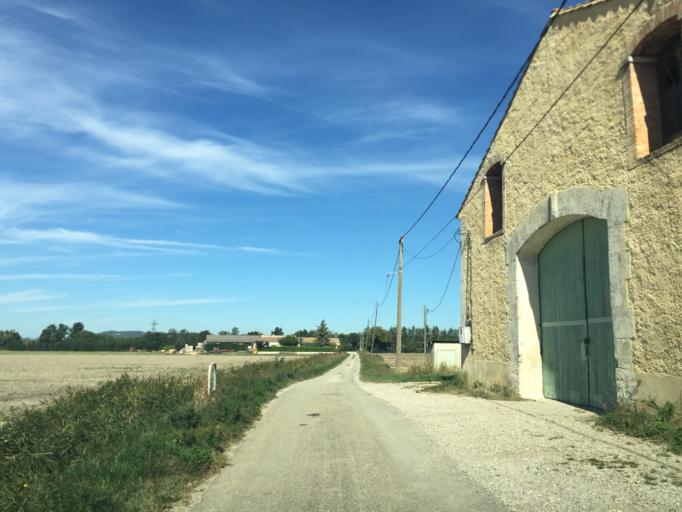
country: FR
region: Provence-Alpes-Cote d'Azur
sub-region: Departement du Vaucluse
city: Piolenc
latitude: 44.1520
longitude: 4.7414
